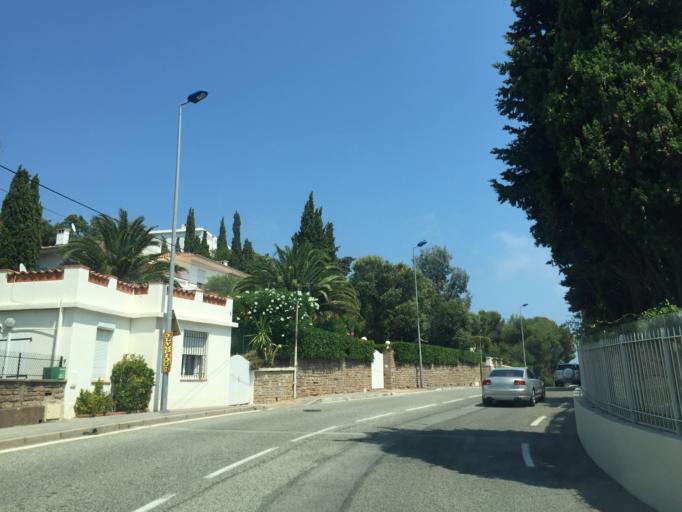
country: FR
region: Provence-Alpes-Cote d'Azur
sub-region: Departement du Var
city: Saint-Raphael
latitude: 43.4273
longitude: 6.8744
